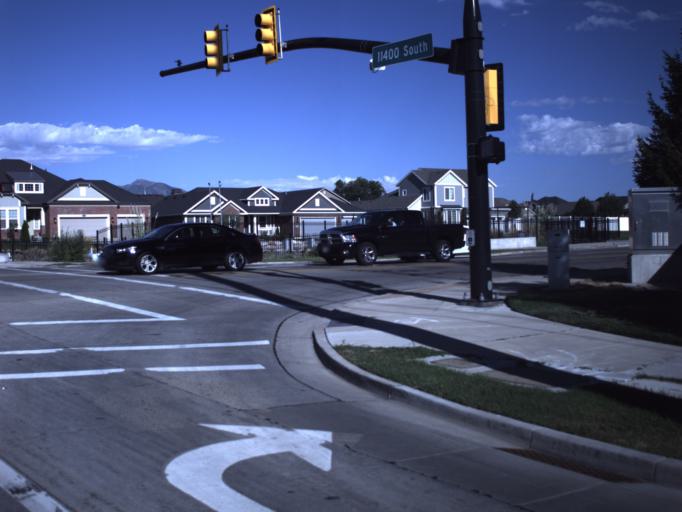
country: US
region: Utah
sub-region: Salt Lake County
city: South Jordan Heights
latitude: 40.5442
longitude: -111.9658
